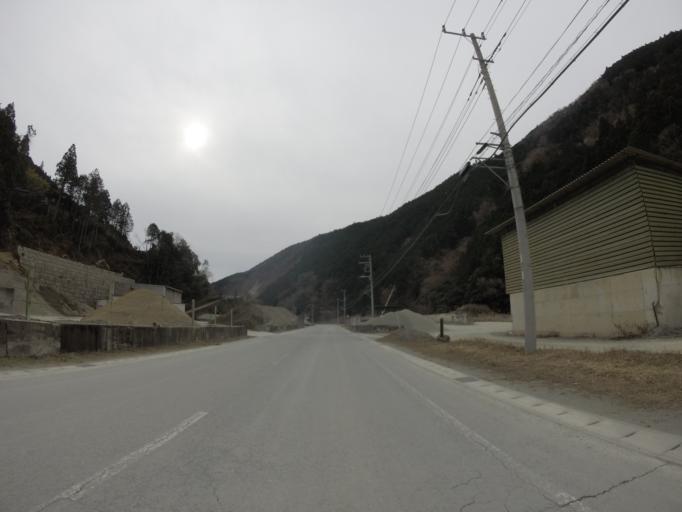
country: JP
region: Shizuoka
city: Fujinomiya
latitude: 35.2448
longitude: 138.5287
